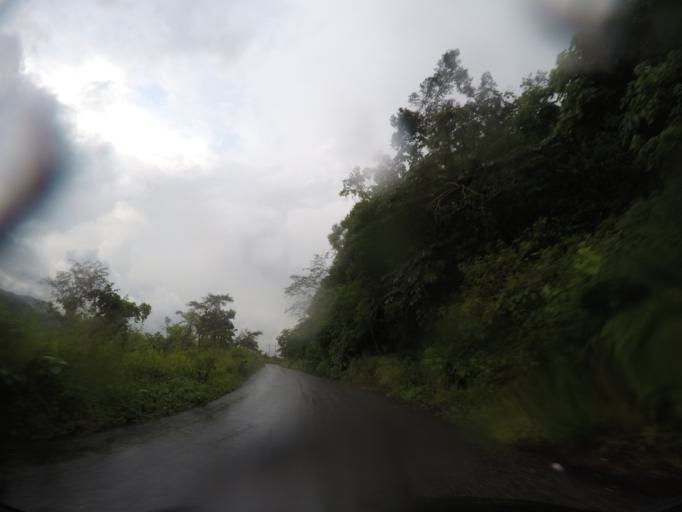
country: MX
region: Oaxaca
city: San Gabriel Mixtepec
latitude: 16.0612
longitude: -97.0756
